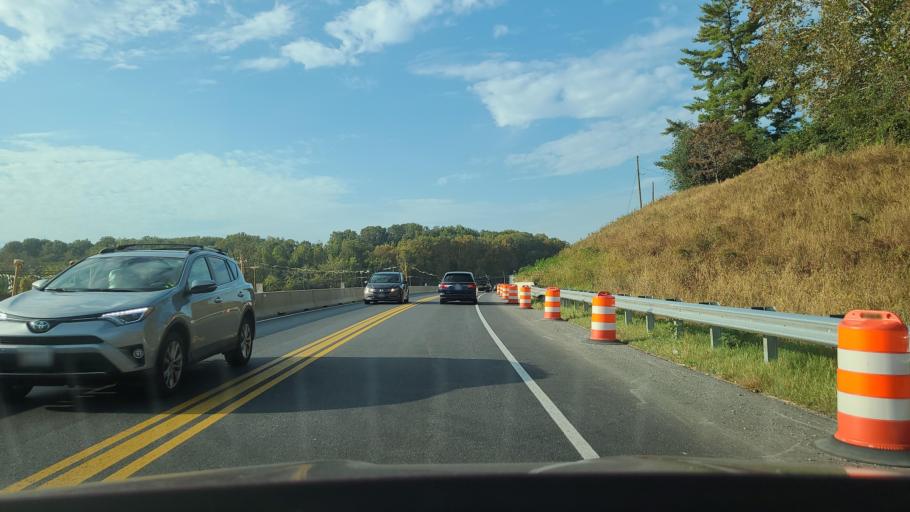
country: US
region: Maryland
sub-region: Carroll County
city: Sykesville
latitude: 39.2908
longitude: -76.9551
